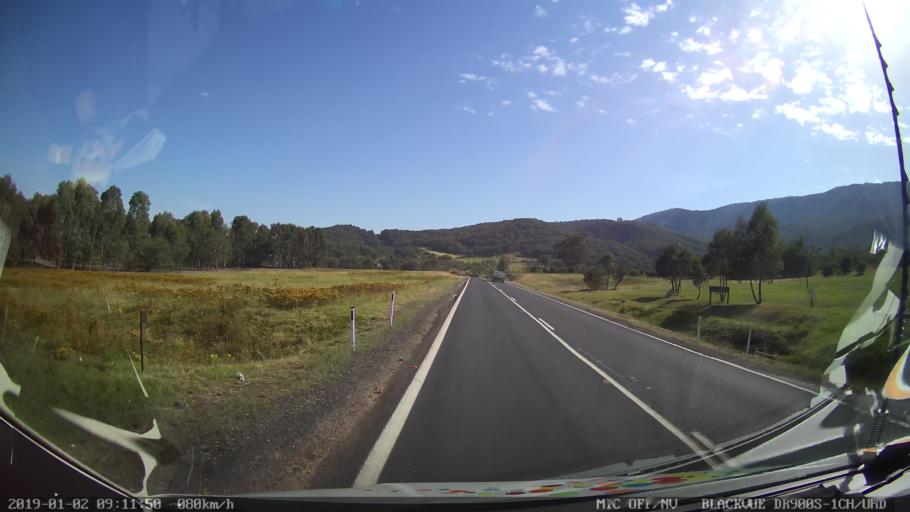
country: AU
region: New South Wales
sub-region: Tumut Shire
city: Tumut
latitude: -35.5077
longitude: 148.2709
